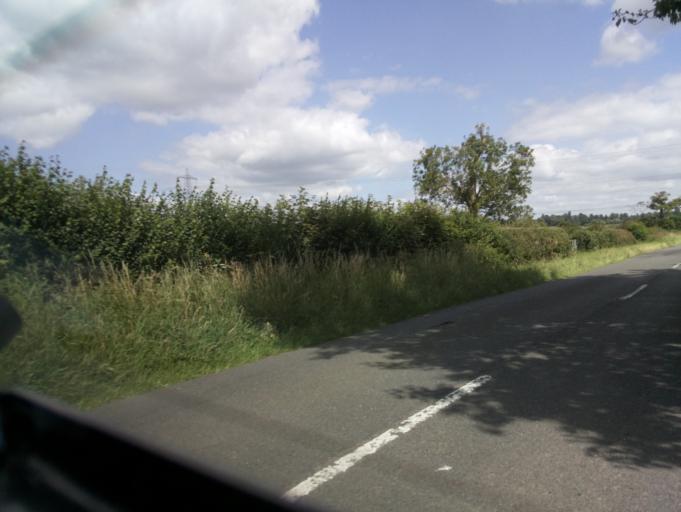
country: GB
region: England
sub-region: Buckinghamshire
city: Winslow
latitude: 51.9232
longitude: -0.8380
